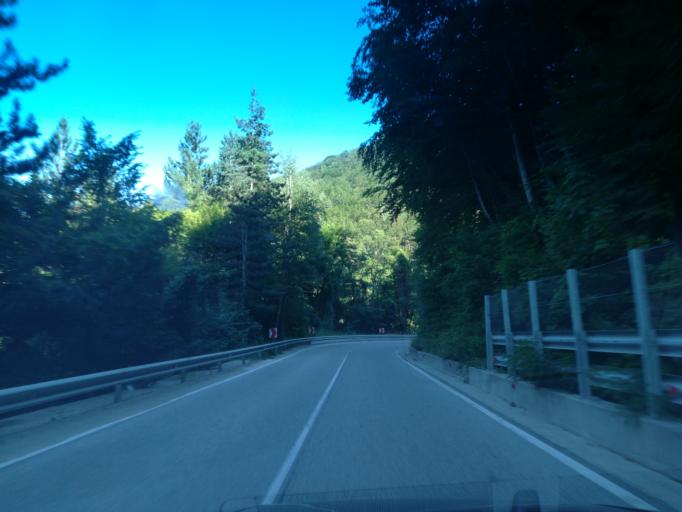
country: BG
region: Smolyan
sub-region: Obshtina Chepelare
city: Chepelare
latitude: 41.8041
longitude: 24.7098
